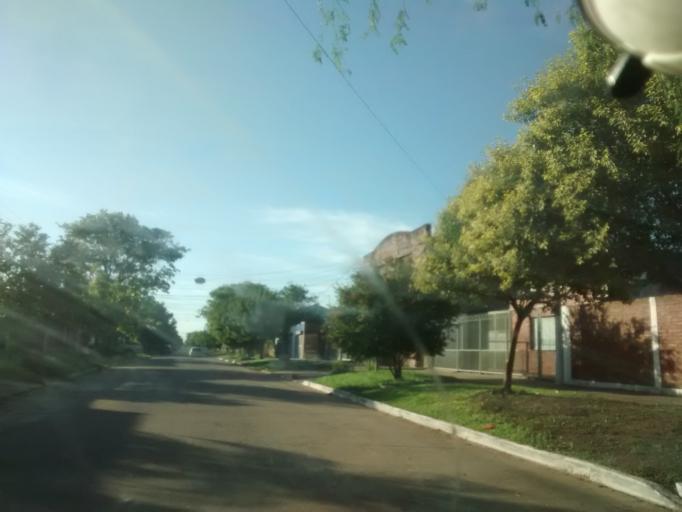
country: AR
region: Chaco
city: Resistencia
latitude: -27.4634
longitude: -58.9997
